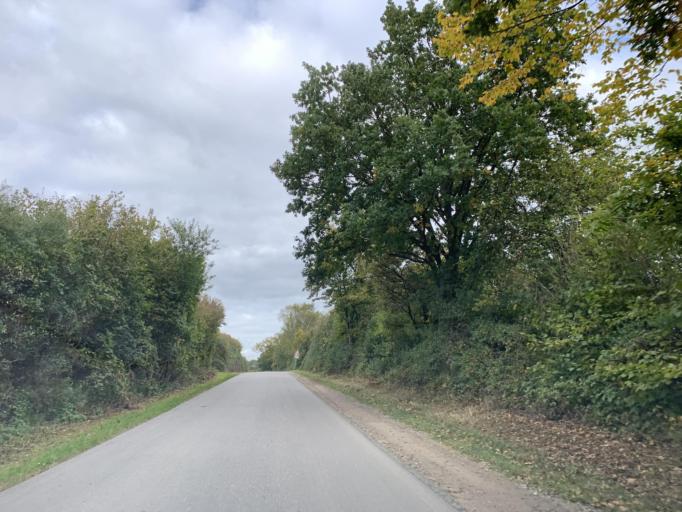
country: DE
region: Mecklenburg-Vorpommern
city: Blankensee
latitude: 53.4215
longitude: 13.2631
